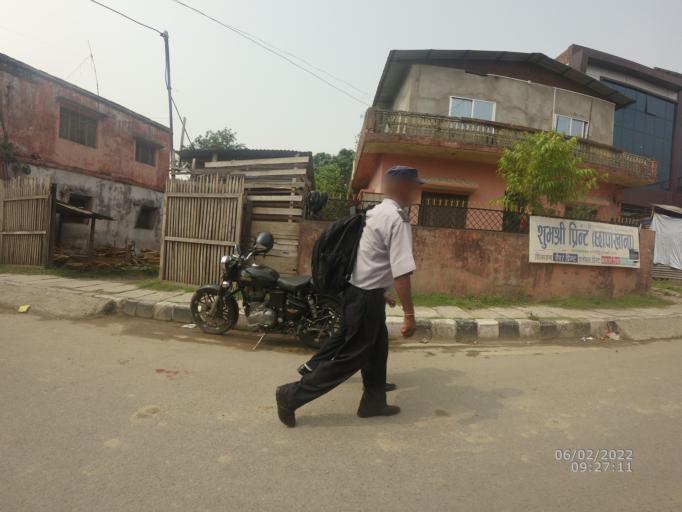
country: NP
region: Western Region
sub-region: Lumbini Zone
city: Bhairahawa
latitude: 27.5006
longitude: 83.4496
